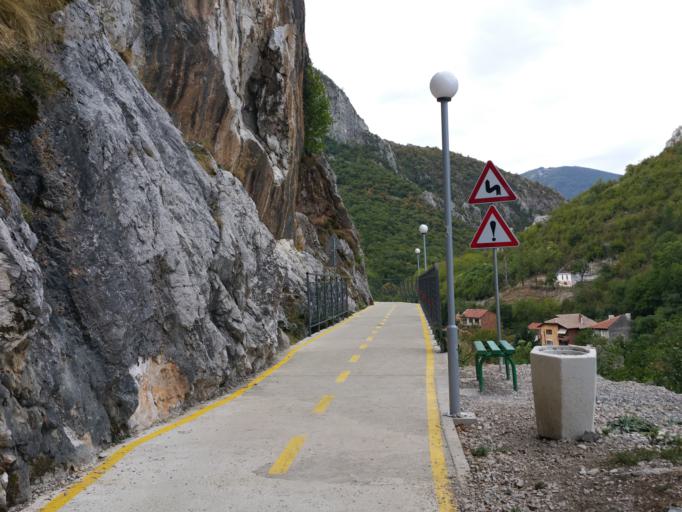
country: BG
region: Vratsa
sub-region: Obshtina Vratsa
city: Vratsa
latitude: 43.1947
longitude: 23.5455
